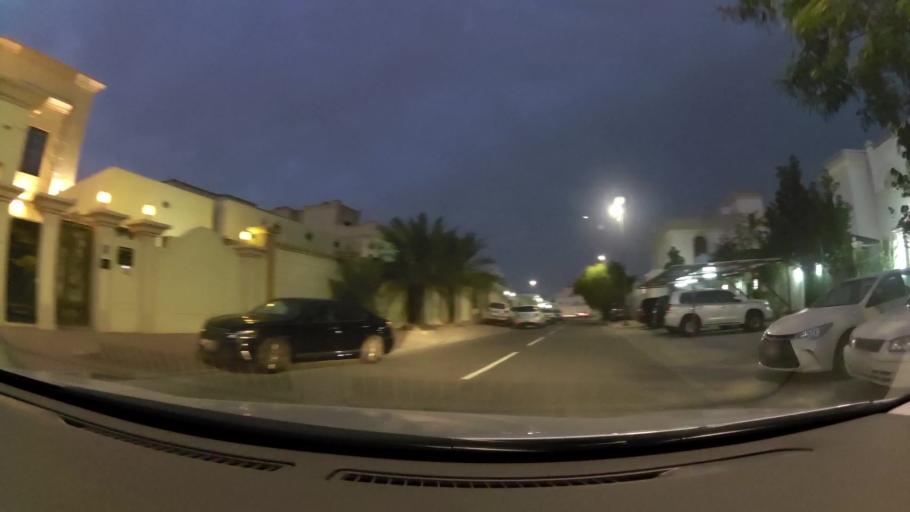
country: QA
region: Baladiyat ad Dawhah
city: Doha
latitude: 25.3451
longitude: 51.5063
